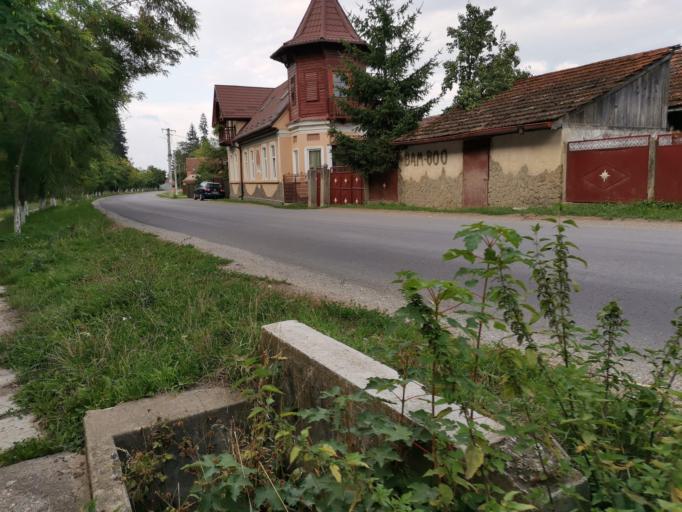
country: RO
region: Brasov
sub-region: Comuna Tarlungeni
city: Zizin
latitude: 45.6400
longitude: 25.7750
